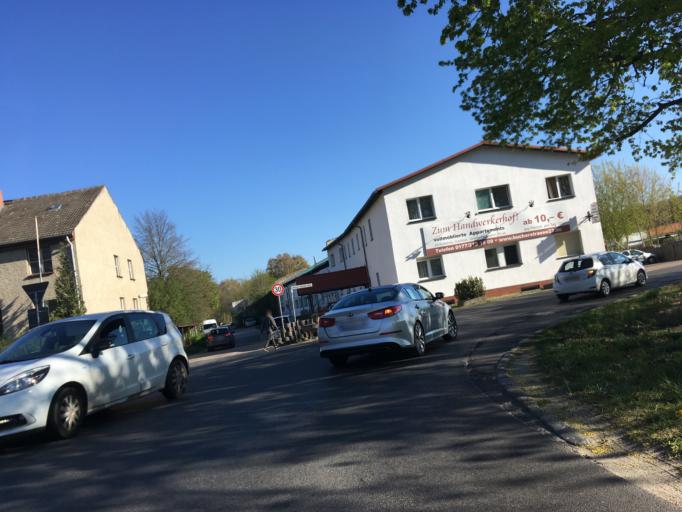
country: DE
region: Brandenburg
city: Bernau bei Berlin
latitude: 52.6914
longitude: 13.5493
